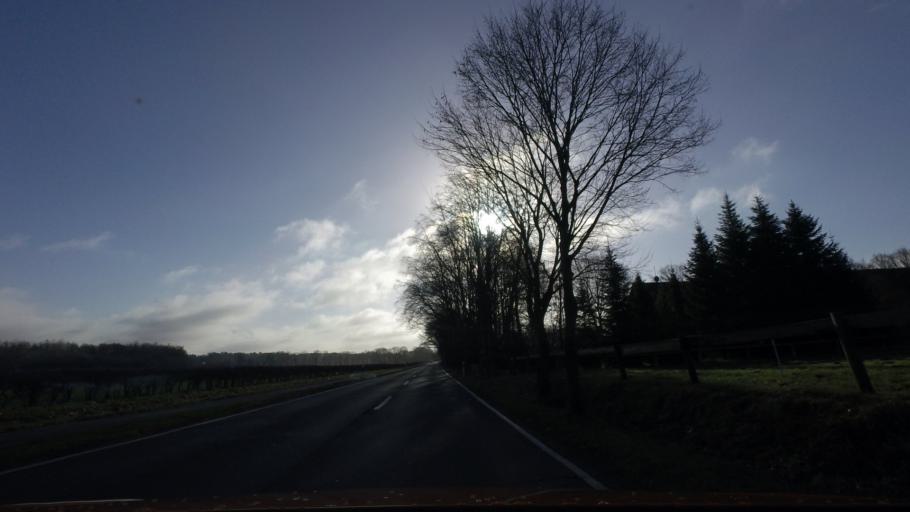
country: DE
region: Lower Saxony
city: Wardenburg
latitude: 53.0224
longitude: 8.2356
